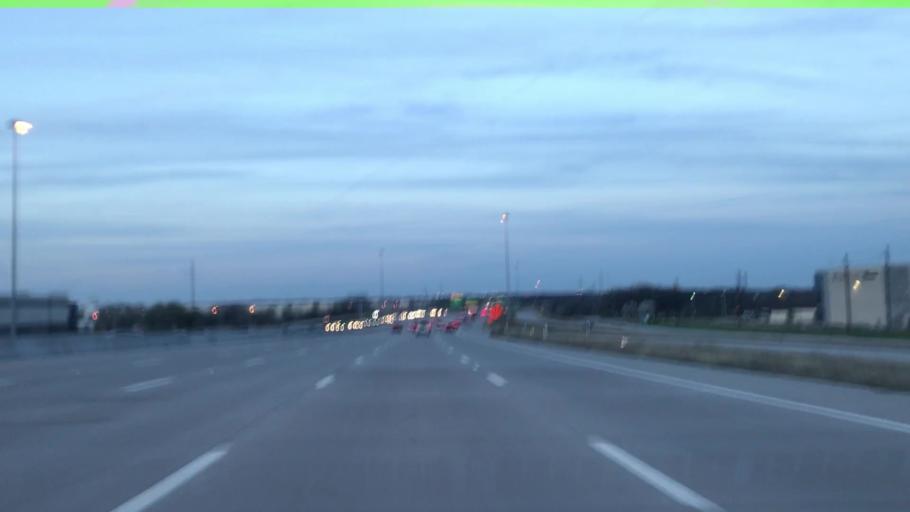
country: US
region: Texas
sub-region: Dallas County
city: Coppell
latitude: 32.9827
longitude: -97.0181
